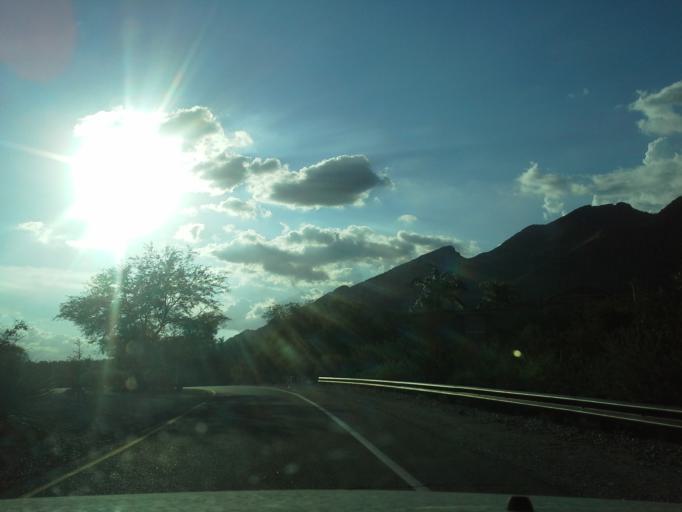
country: US
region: Arizona
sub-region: Pima County
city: Catalina Foothills
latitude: 32.3284
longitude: -110.8620
